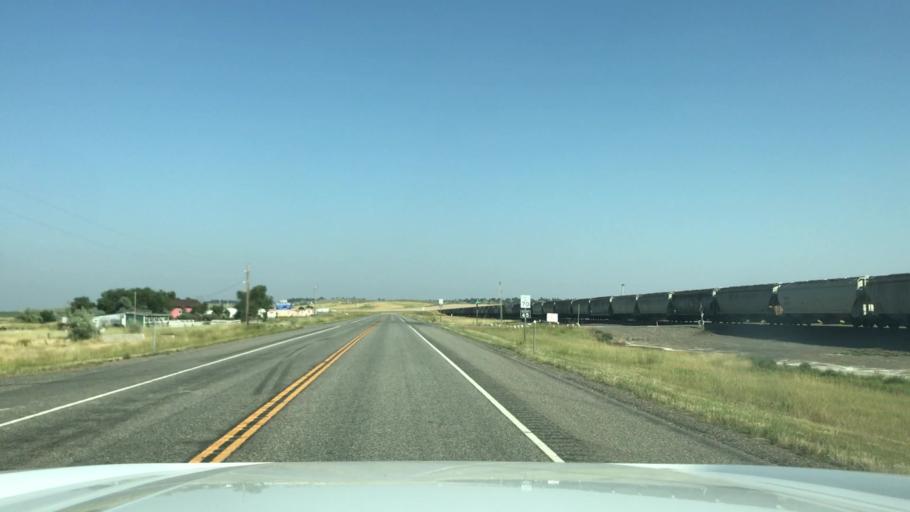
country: US
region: Montana
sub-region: Yellowstone County
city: Billings
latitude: 45.9324
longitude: -108.6845
